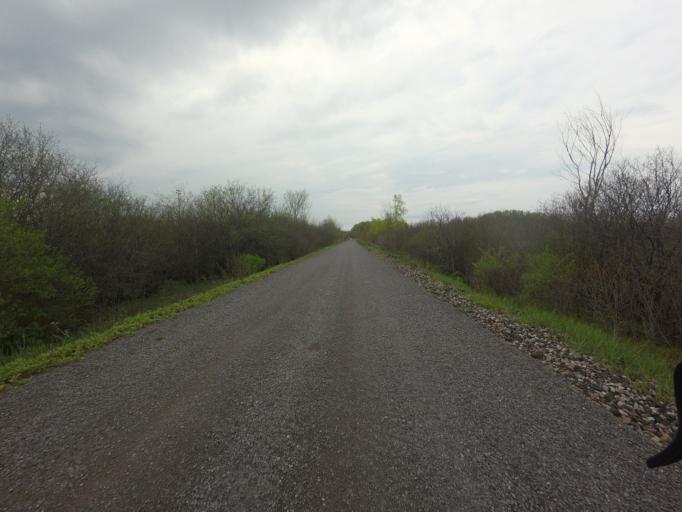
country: CA
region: Ontario
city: Carleton Place
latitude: 45.2180
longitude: -76.1846
